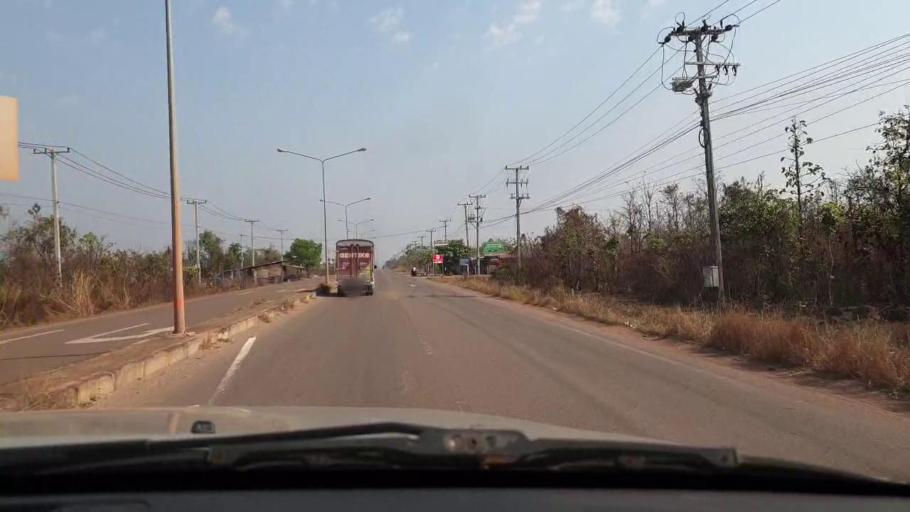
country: LA
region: Vientiane
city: Vientiane
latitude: 18.0156
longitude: 102.7239
